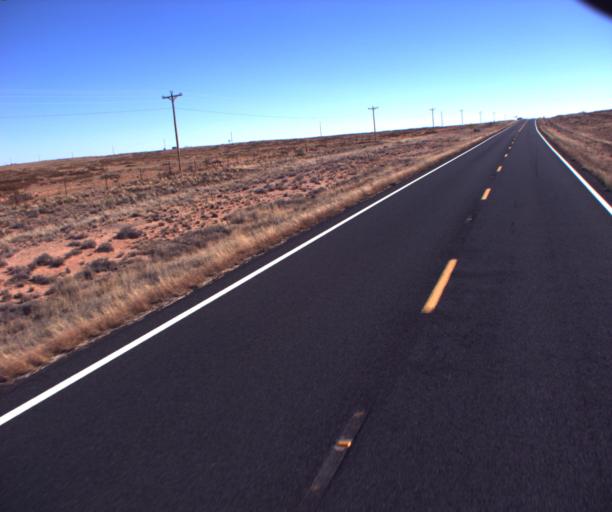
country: US
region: Arizona
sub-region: Coconino County
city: Tuba City
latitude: 36.0093
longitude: -111.0626
